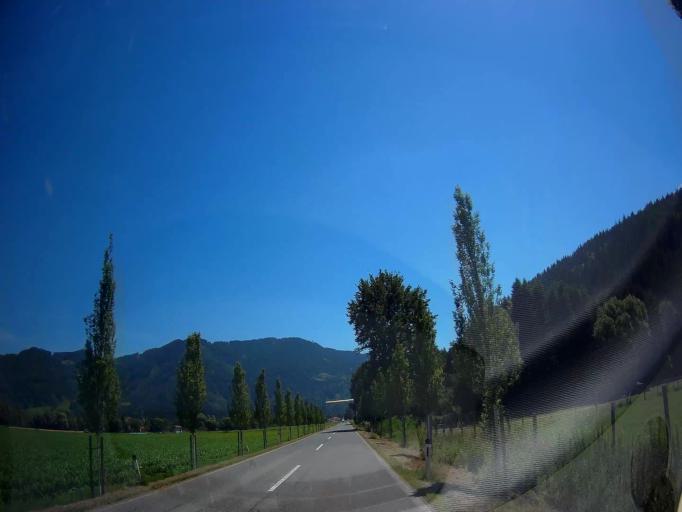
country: AT
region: Carinthia
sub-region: Politischer Bezirk Sankt Veit an der Glan
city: Friesach
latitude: 46.9451
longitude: 14.4145
